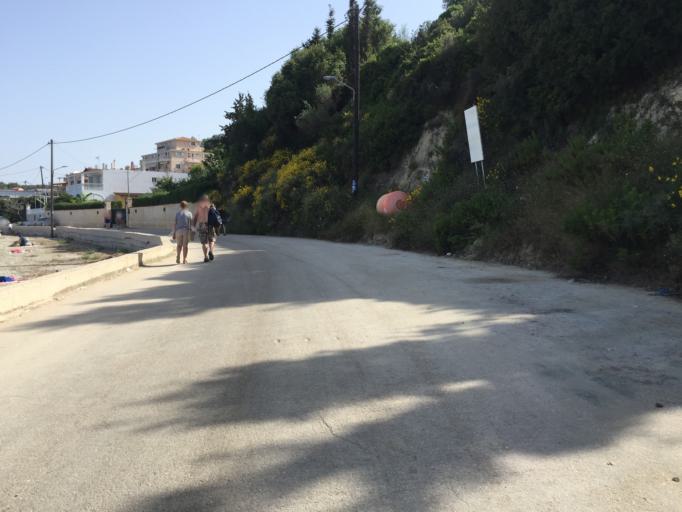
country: GR
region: Ionian Islands
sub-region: Nomos Zakynthou
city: Vanaton
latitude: 37.8202
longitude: 20.8666
